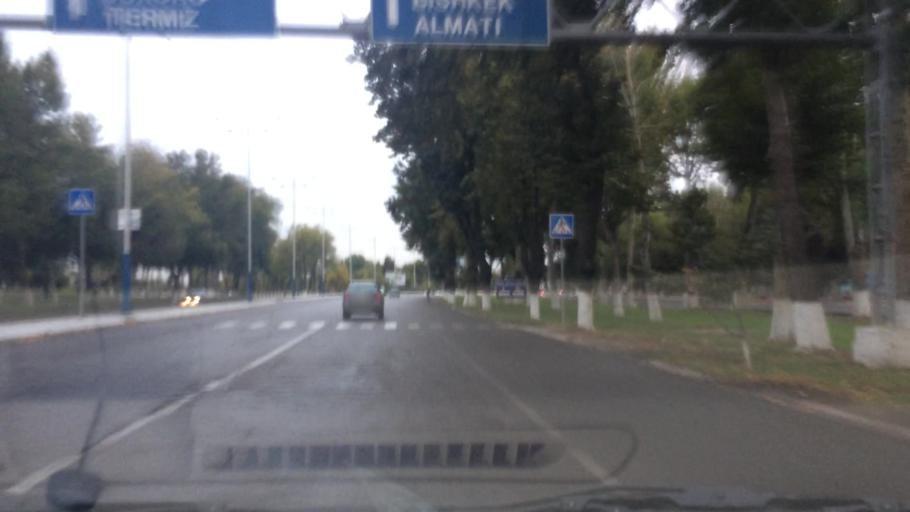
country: UZ
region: Toshkent Shahri
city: Tashkent
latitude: 41.2601
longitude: 69.1965
